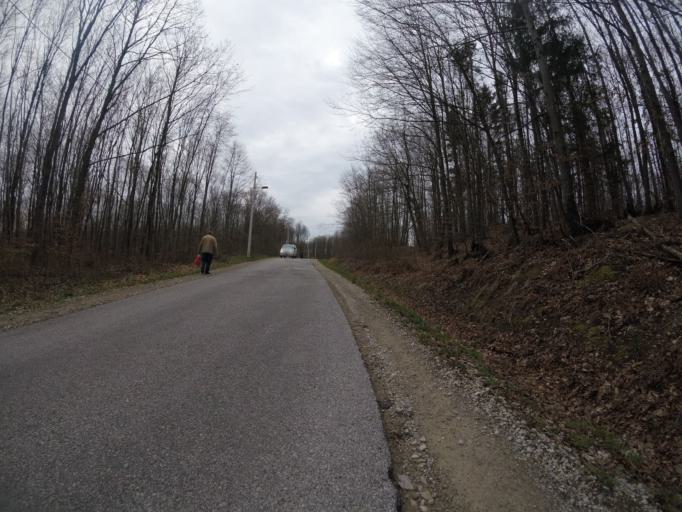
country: HR
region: Grad Zagreb
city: Strmec
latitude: 45.6360
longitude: 15.9338
